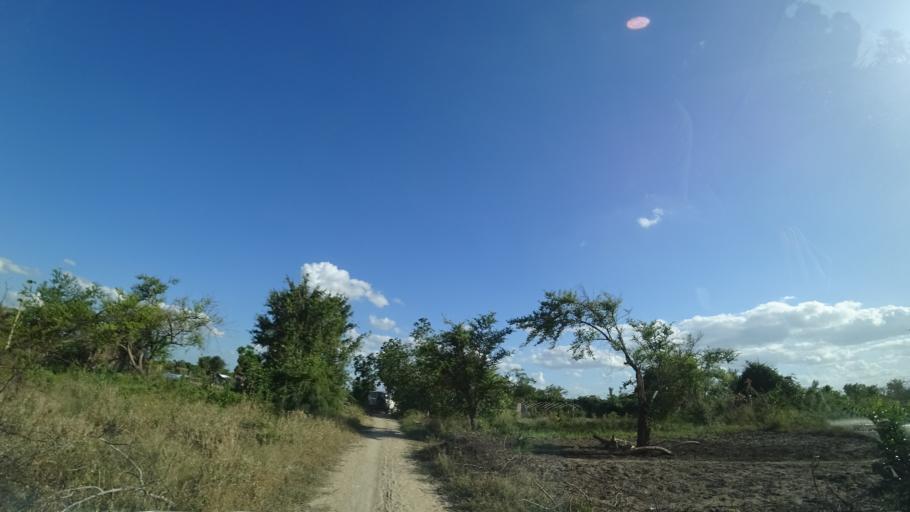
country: MZ
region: Sofala
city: Dondo
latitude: -19.3533
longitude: 34.5878
